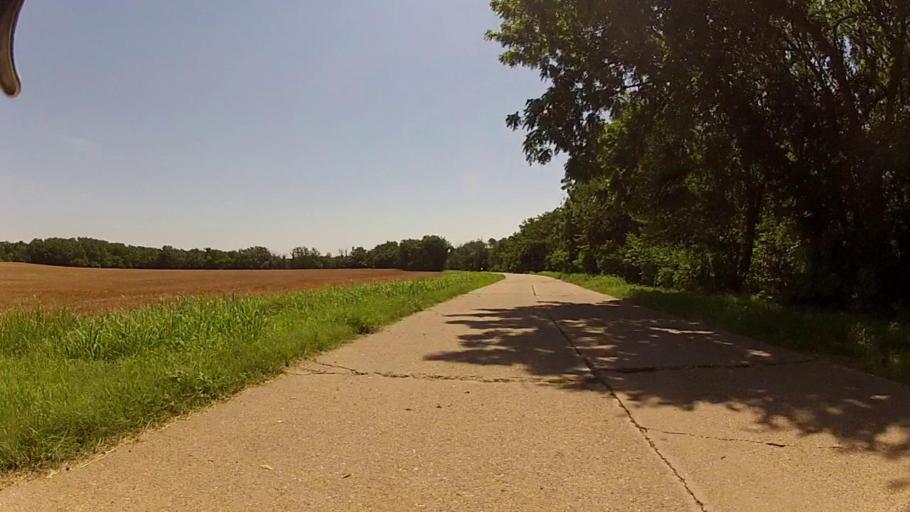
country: US
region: Kansas
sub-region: Sumner County
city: Caldwell
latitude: 37.0340
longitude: -97.4888
